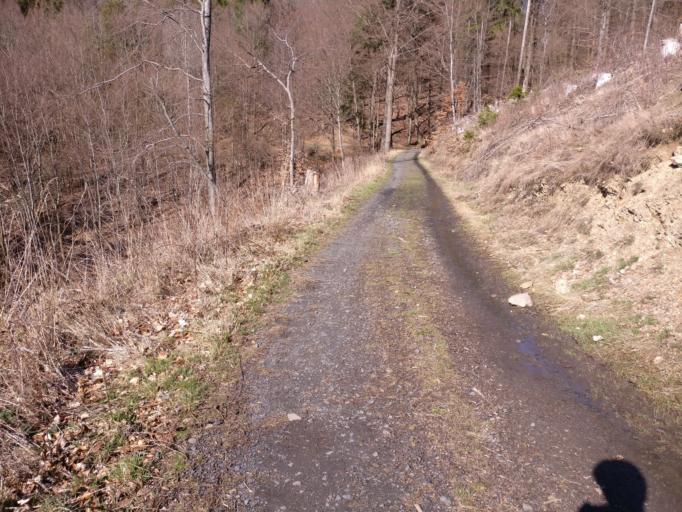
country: DE
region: Hesse
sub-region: Regierungsbezirk Giessen
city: Greifenstein
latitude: 50.6111
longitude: 8.2775
